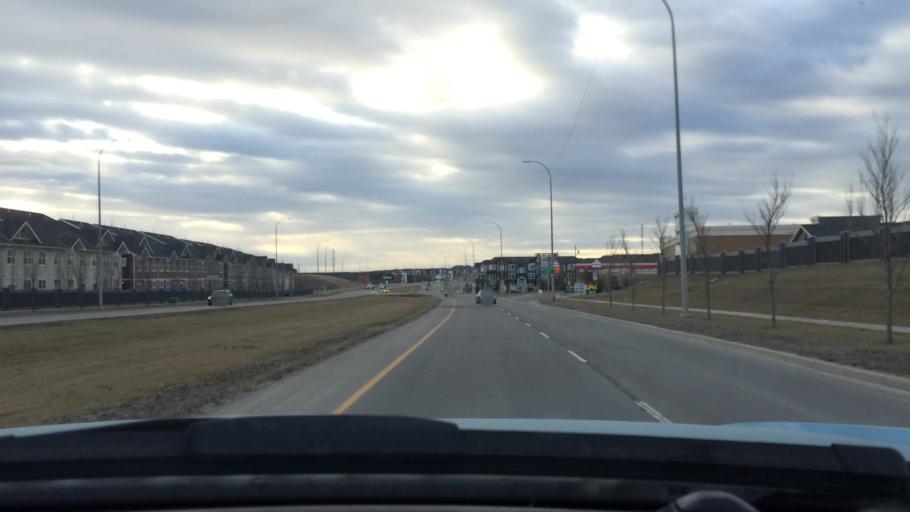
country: CA
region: Alberta
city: Calgary
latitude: 51.1747
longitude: -114.1566
